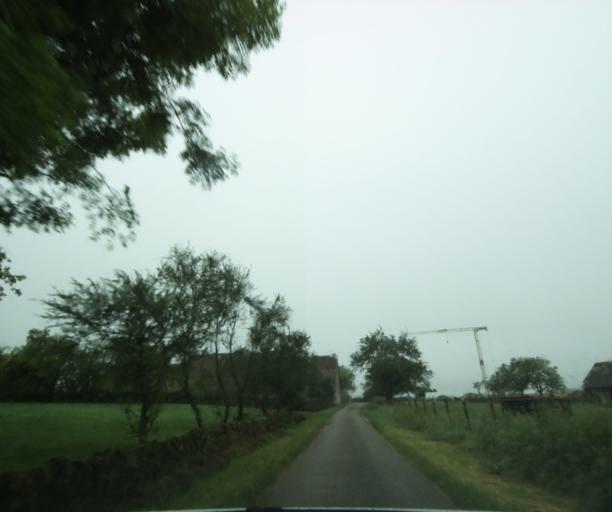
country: FR
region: Bourgogne
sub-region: Departement de Saone-et-Loire
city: Charolles
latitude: 46.3920
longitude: 4.2297
